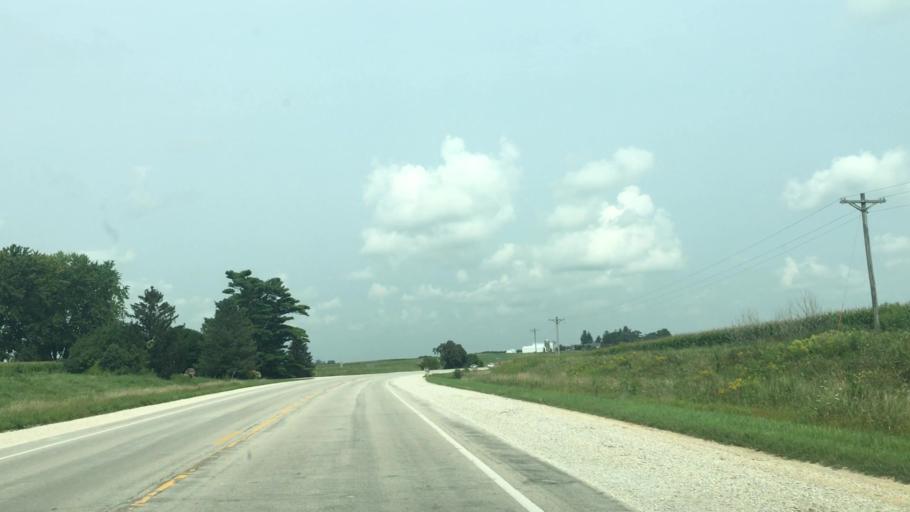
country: US
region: Iowa
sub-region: Winneshiek County
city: Decorah
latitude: 43.4124
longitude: -91.8580
